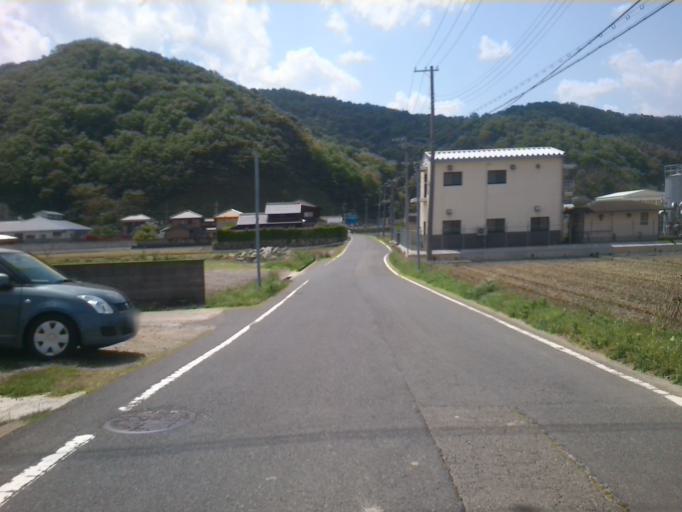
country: JP
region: Kyoto
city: Miyazu
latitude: 35.7290
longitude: 135.1013
